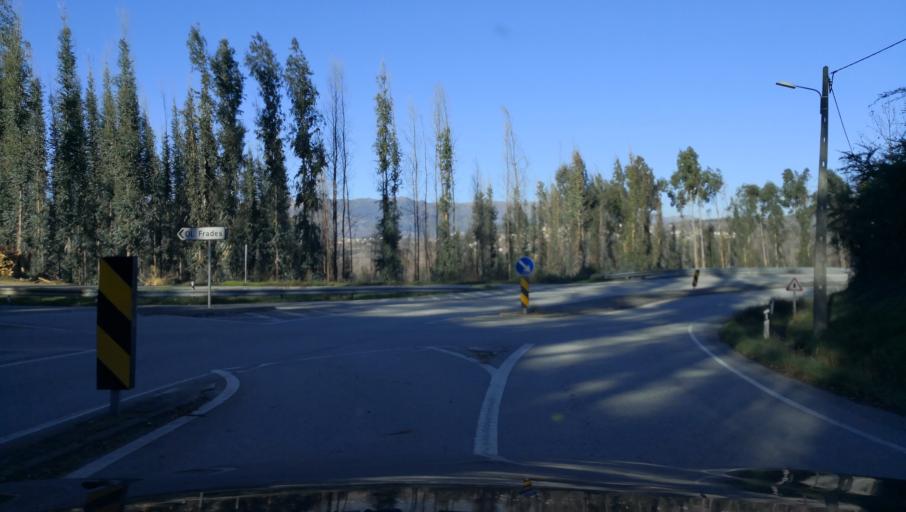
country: PT
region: Viseu
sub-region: Vouzela
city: Vouzela
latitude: 40.7278
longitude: -8.1257
